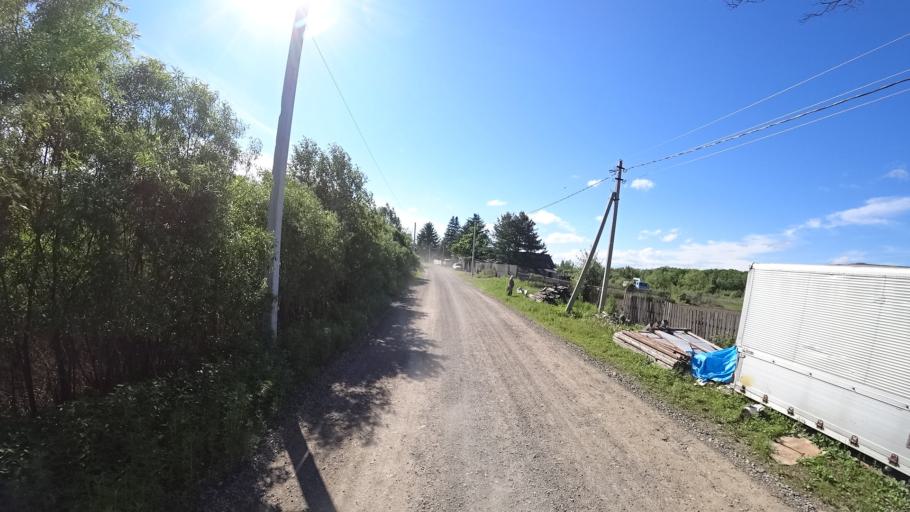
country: RU
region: Khabarovsk Krai
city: Khor
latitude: 47.8862
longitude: 135.0160
